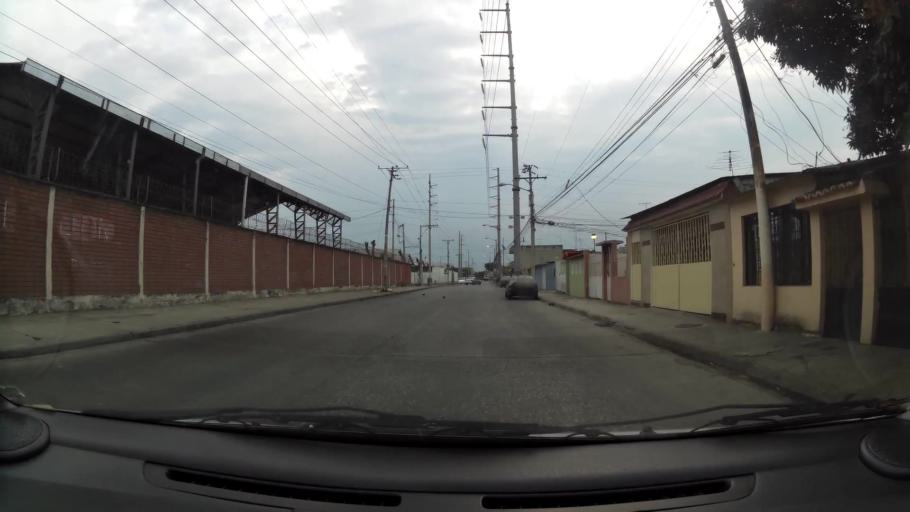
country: EC
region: Guayas
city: Guayaquil
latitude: -2.2417
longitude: -79.8863
